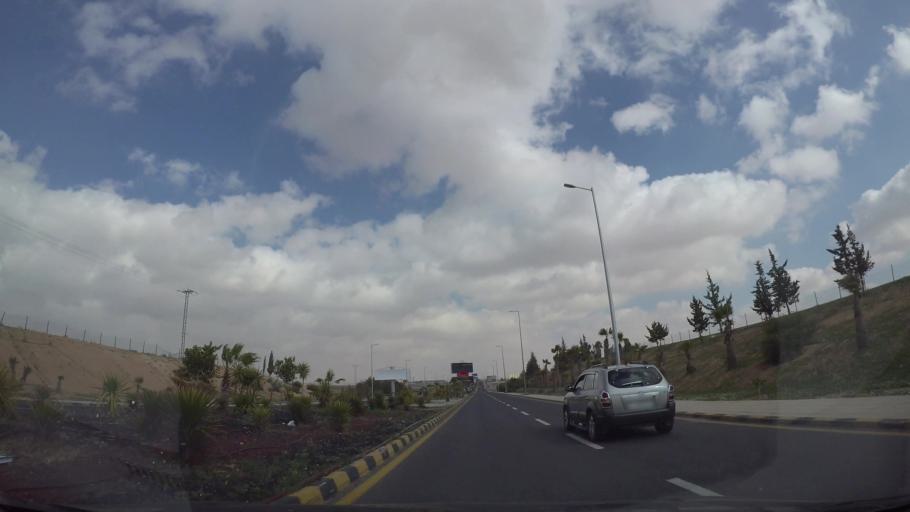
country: JO
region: Amman
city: Al Jizah
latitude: 31.7226
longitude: 35.9523
